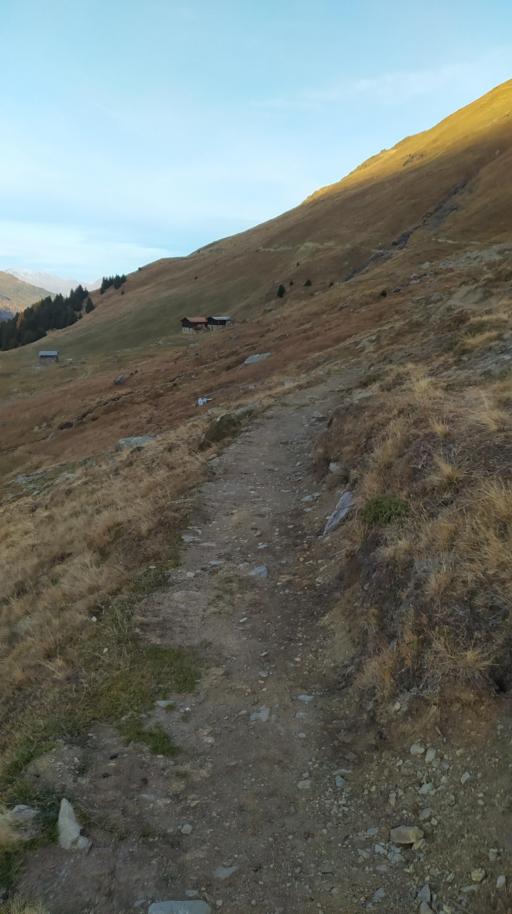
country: IT
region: Lombardy
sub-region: Provincia di Sondrio
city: Sant'Antonio
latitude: 46.4209
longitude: 10.5049
